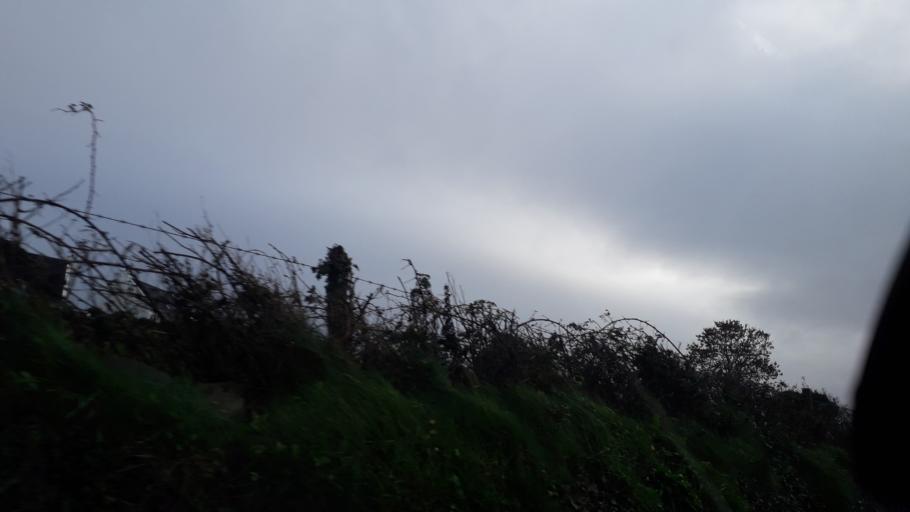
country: IE
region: Ulster
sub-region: County Donegal
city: Buncrana
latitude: 55.1032
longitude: -7.5346
